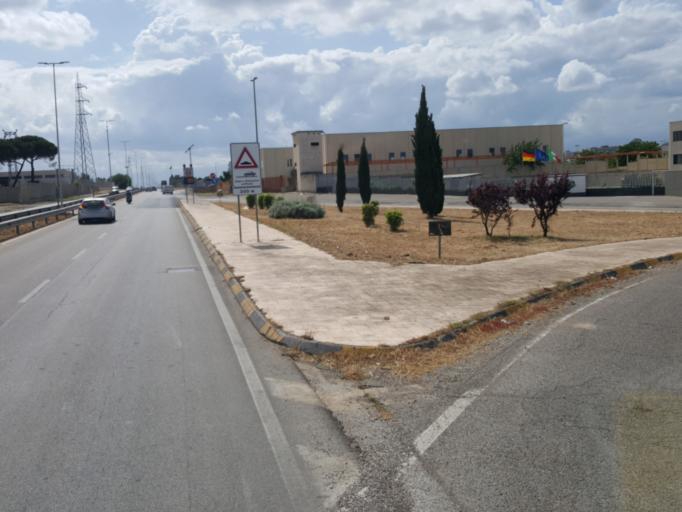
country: IT
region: Apulia
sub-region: Provincia di Bari
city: San Paolo
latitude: 41.1133
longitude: 16.7991
